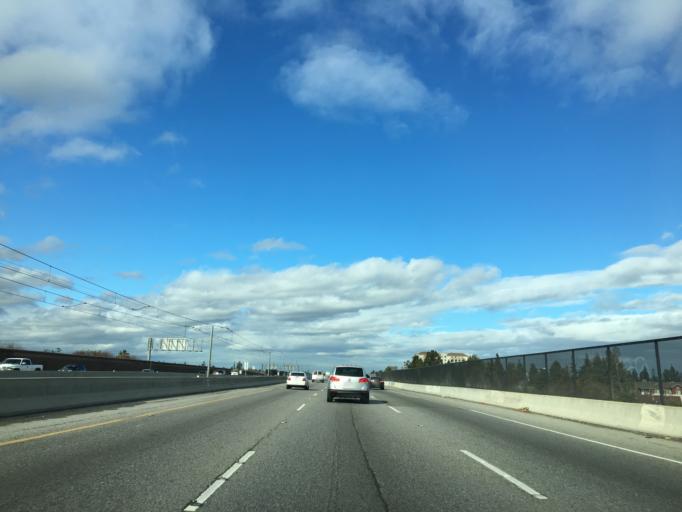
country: US
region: California
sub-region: Santa Clara County
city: San Jose
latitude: 37.3059
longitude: -121.8798
